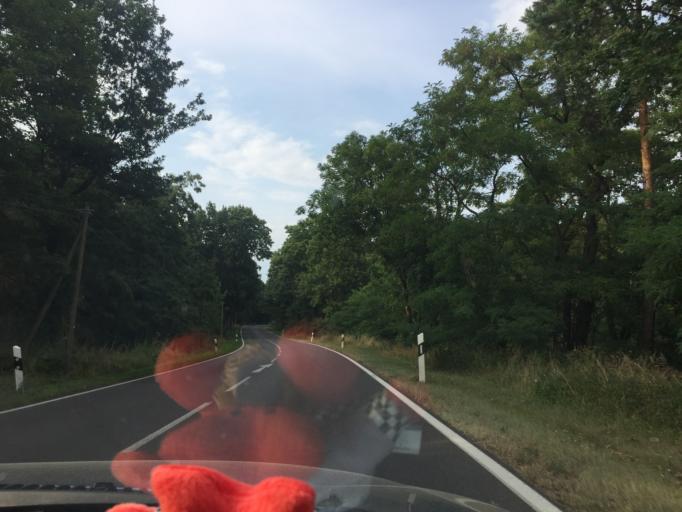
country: DE
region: Brandenburg
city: Liebenwalde
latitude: 52.8806
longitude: 13.3971
